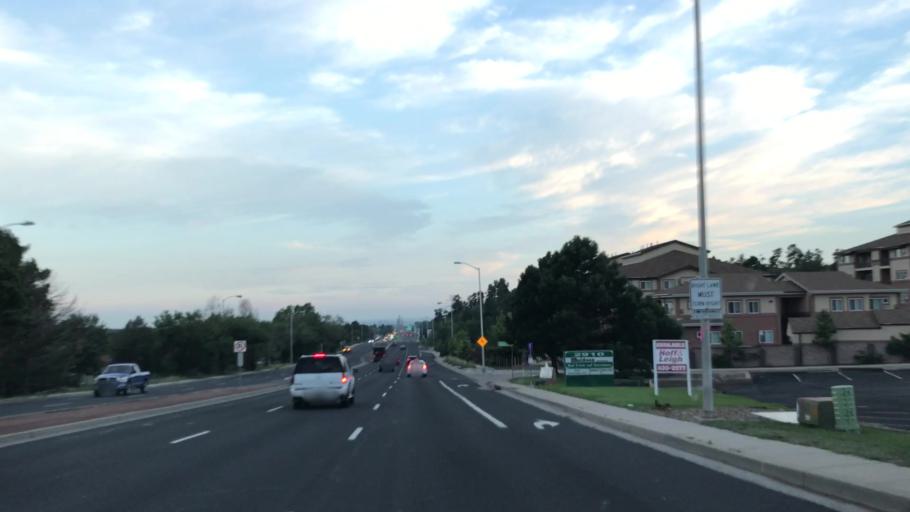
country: US
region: Colorado
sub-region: El Paso County
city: Cimarron Hills
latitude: 38.8745
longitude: -104.7572
